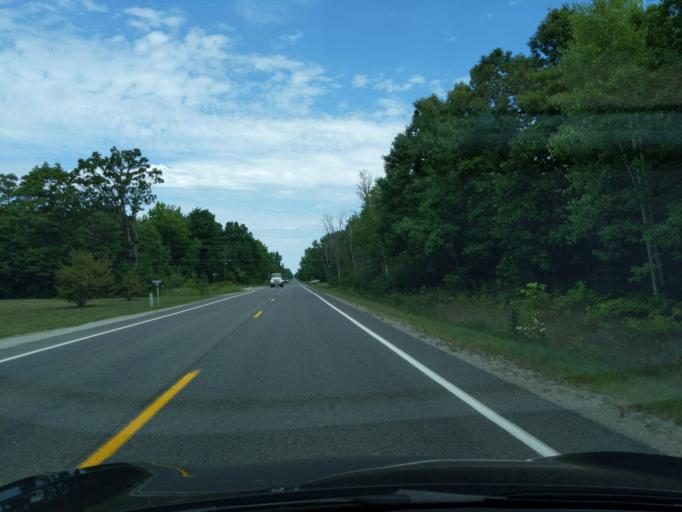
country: US
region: Michigan
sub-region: Midland County
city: Midland
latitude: 43.5376
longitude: -84.3697
